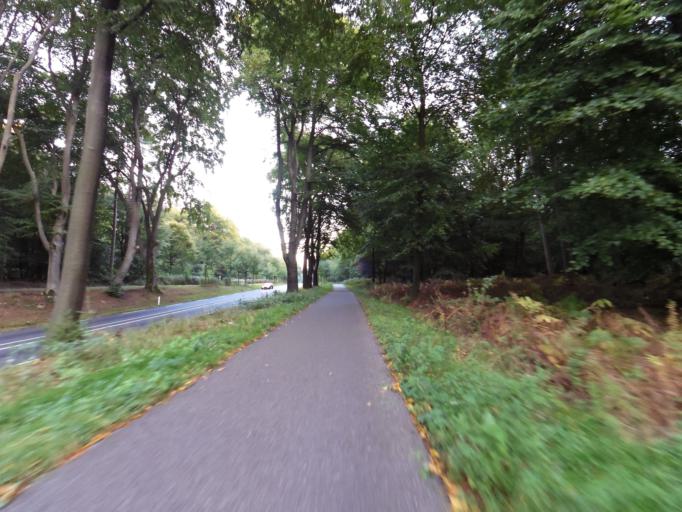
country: NL
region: Gelderland
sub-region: Gemeente Montferland
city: s-Heerenberg
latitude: 51.9088
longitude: 6.2170
